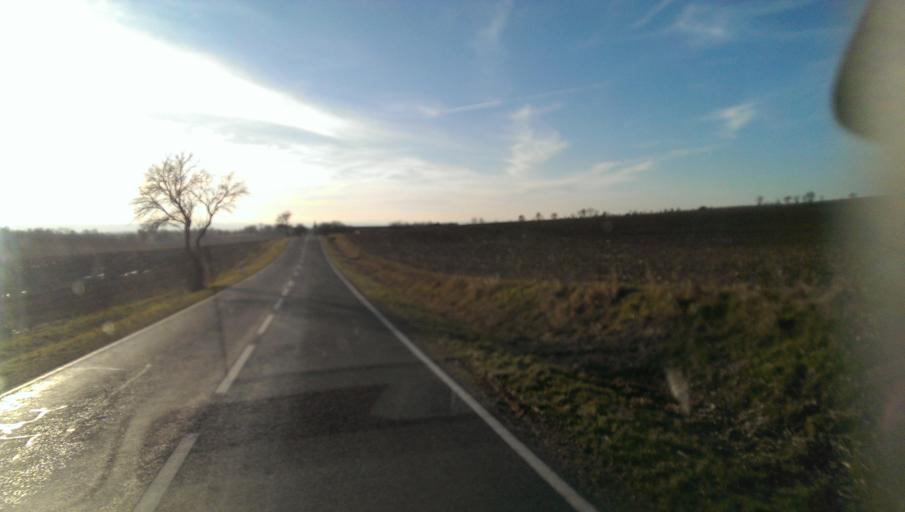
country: DE
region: Saxony-Anhalt
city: Hornhausen
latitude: 52.1000
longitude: 11.1698
